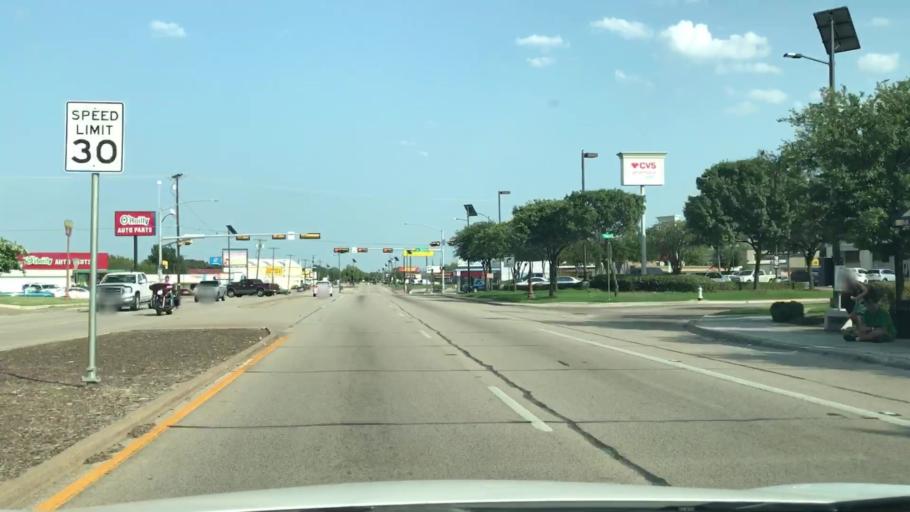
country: US
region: Texas
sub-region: Dallas County
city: Irving
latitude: 32.8121
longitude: -96.9354
